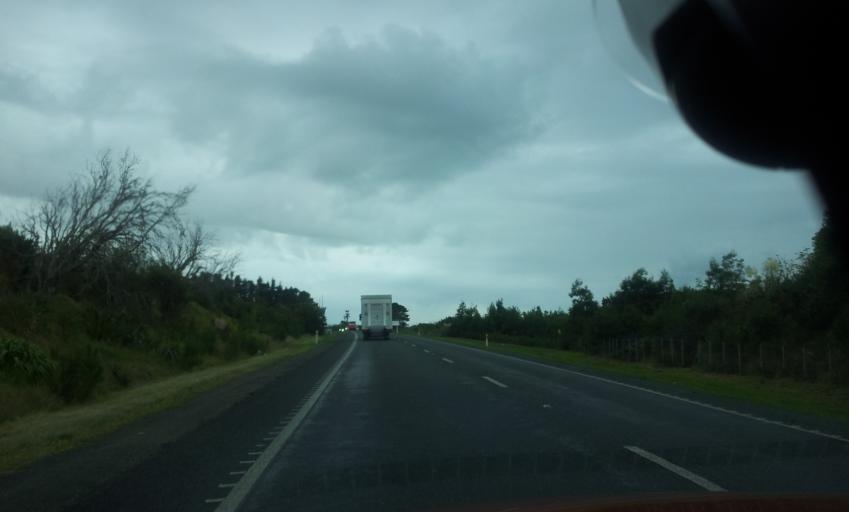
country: NZ
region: Northland
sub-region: Whangarei
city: Ruakaka
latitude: -35.9388
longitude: 174.4560
